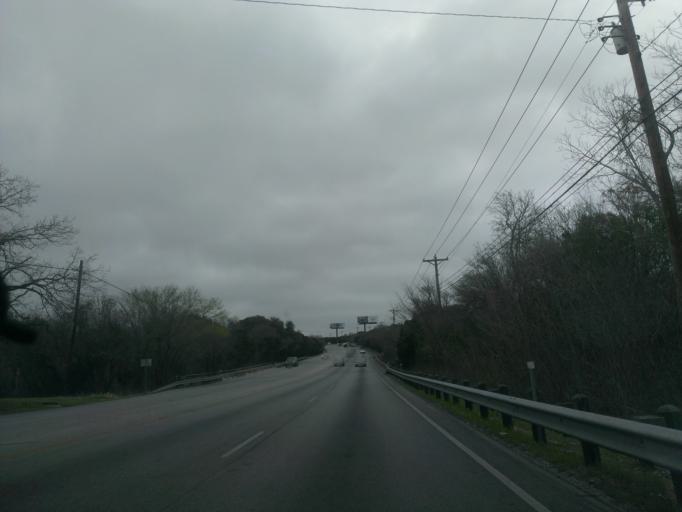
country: US
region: Texas
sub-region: Travis County
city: Wells Branch
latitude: 30.3943
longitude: -97.6808
